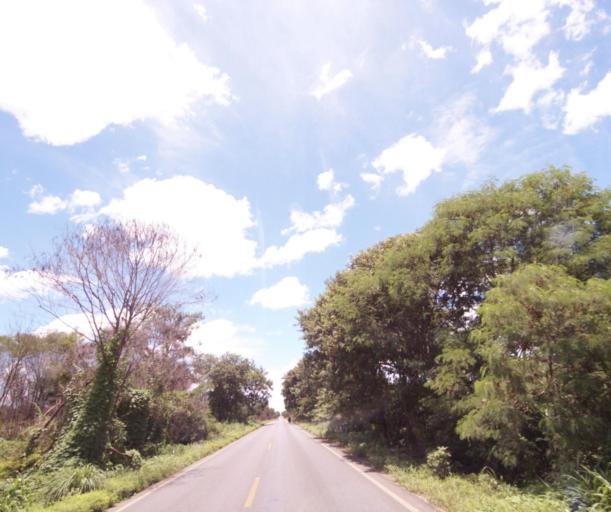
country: BR
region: Bahia
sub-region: Bom Jesus Da Lapa
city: Bom Jesus da Lapa
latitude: -13.2643
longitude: -43.5703
